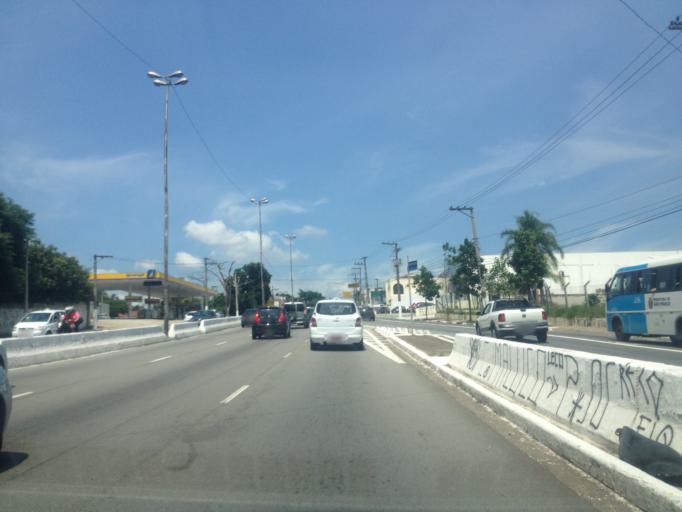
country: BR
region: Sao Paulo
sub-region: Diadema
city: Diadema
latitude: -23.6456
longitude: -46.6738
